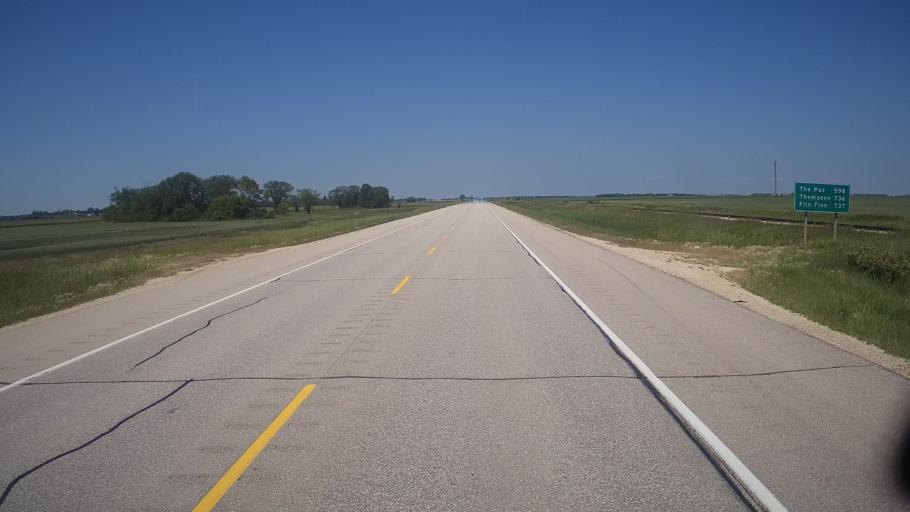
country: CA
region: Manitoba
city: Stonewall
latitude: 50.0123
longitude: -97.3630
